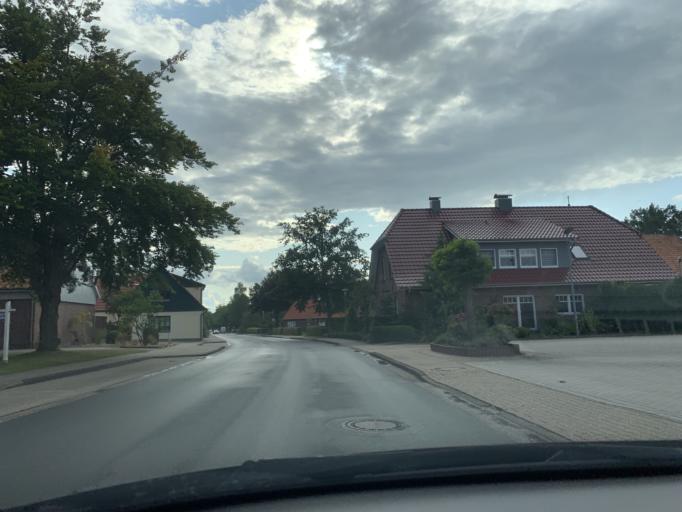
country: DE
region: Lower Saxony
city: Westerstede
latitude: 53.3156
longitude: 7.9233
